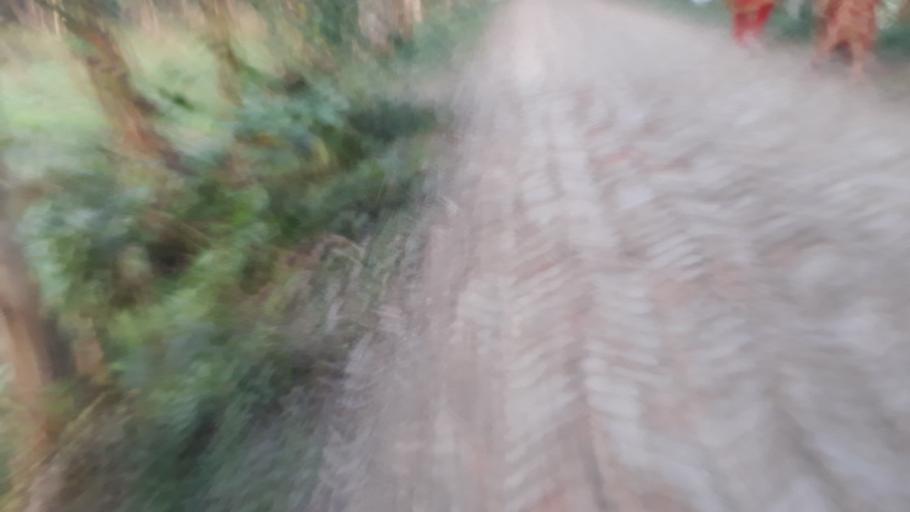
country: BD
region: Khulna
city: Kaliganj
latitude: 23.3579
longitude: 88.9113
